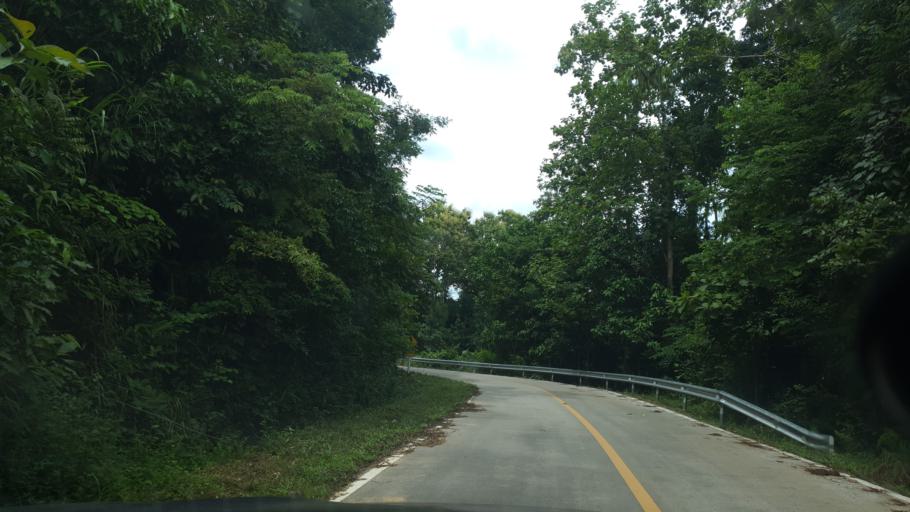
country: TH
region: Lampang
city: Hang Chat
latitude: 18.3635
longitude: 99.2608
